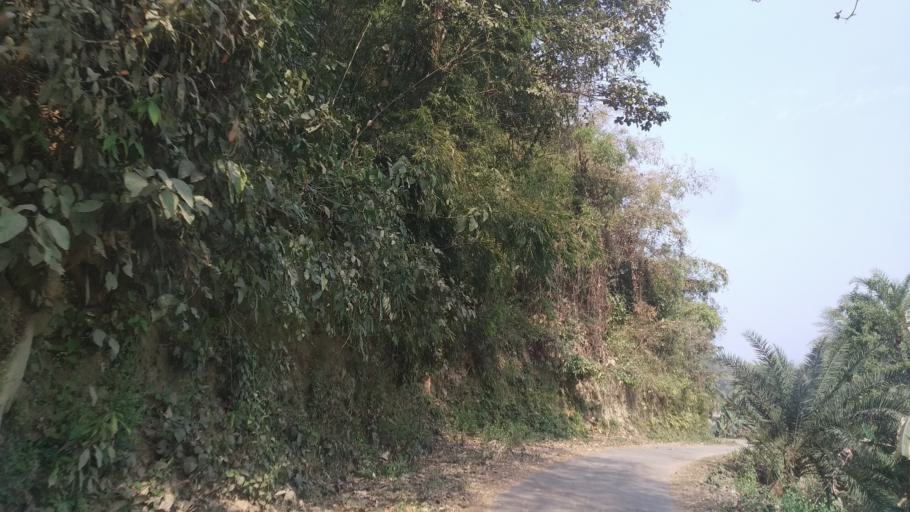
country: IN
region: Tripura
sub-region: West Tripura
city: Sonamura
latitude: 23.5223
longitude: 91.2577
